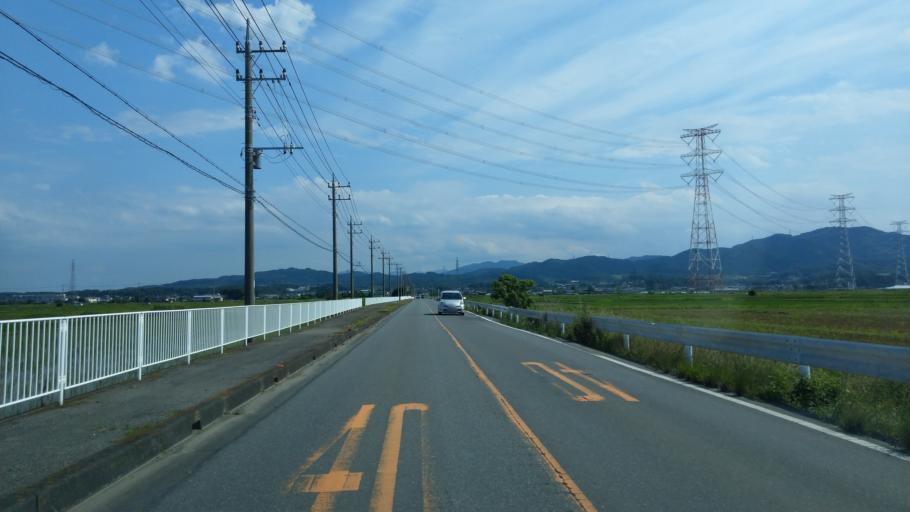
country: JP
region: Saitama
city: Kodamacho-kodamaminami
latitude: 36.1913
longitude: 139.1690
